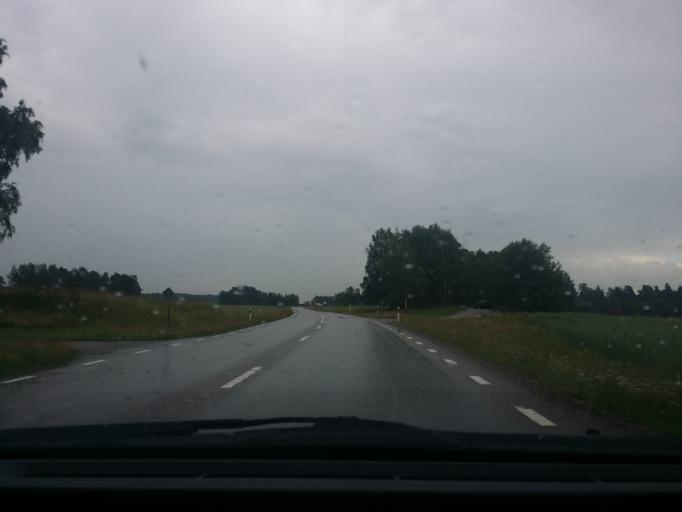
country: SE
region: OErebro
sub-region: Lindesbergs Kommun
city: Fellingsbro
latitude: 59.4524
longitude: 15.5834
